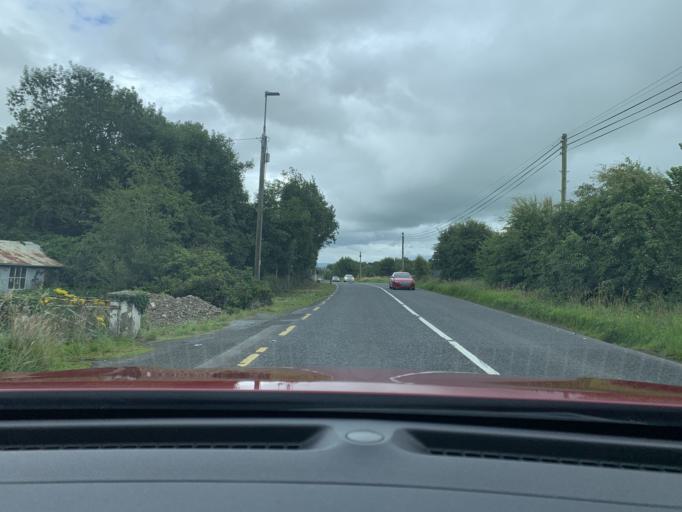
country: IE
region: Ulster
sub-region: County Donegal
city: Convoy
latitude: 54.8006
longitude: -7.6333
